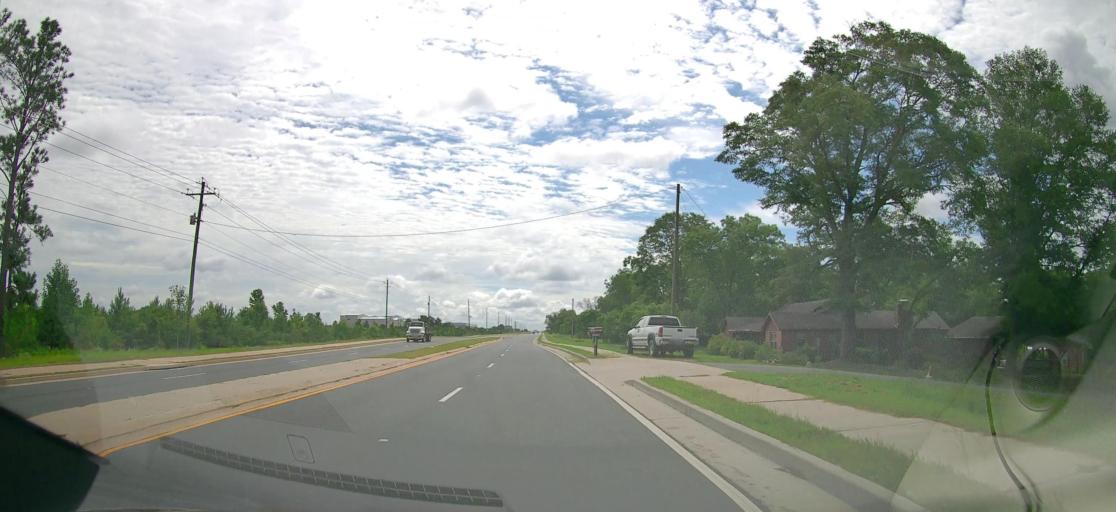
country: US
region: Georgia
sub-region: Houston County
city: Centerville
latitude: 32.6835
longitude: -83.6536
